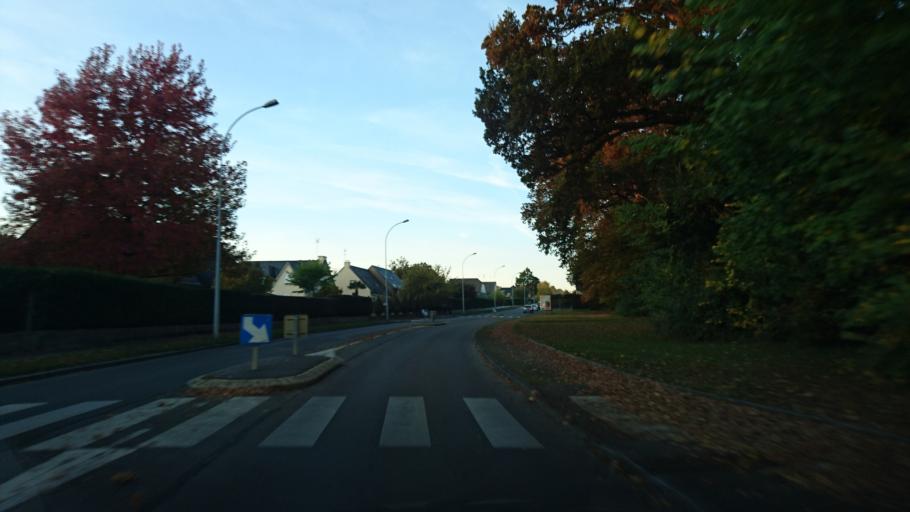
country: FR
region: Brittany
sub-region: Departement d'Ille-et-Vilaine
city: Bruz
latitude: 48.0217
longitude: -1.7524
